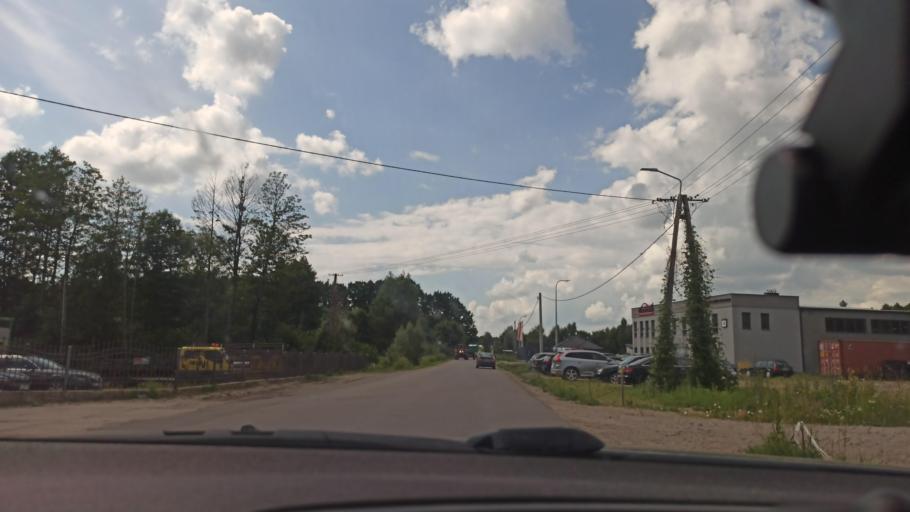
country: PL
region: Podlasie
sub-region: Powiat bialostocki
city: Turosn Koscielna
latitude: 53.0648
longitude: 23.0950
